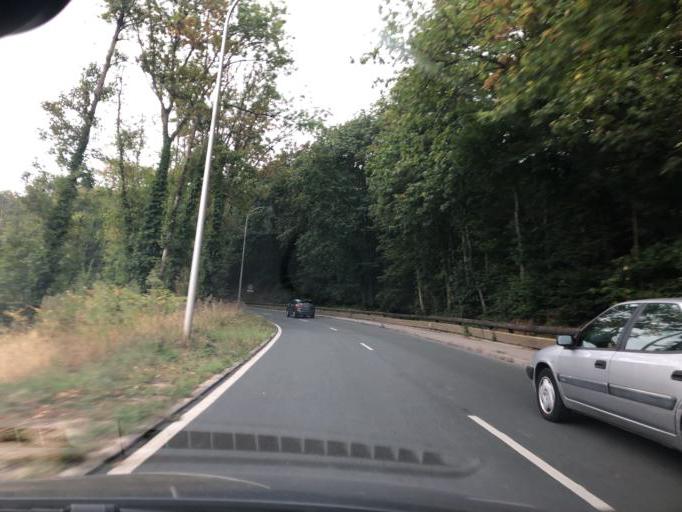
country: FR
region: Ile-de-France
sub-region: Departement des Hauts-de-Seine
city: Chaville
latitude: 48.7932
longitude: 2.1776
